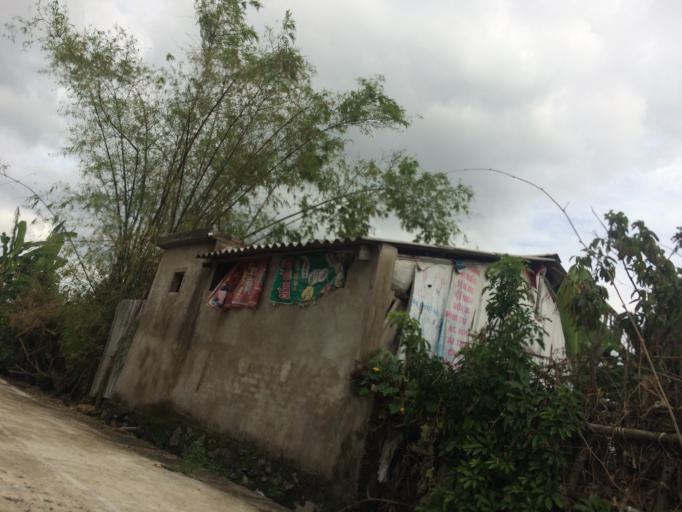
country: VN
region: Ha Tinh
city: Ha Tinh
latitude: 18.3341
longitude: 105.9178
